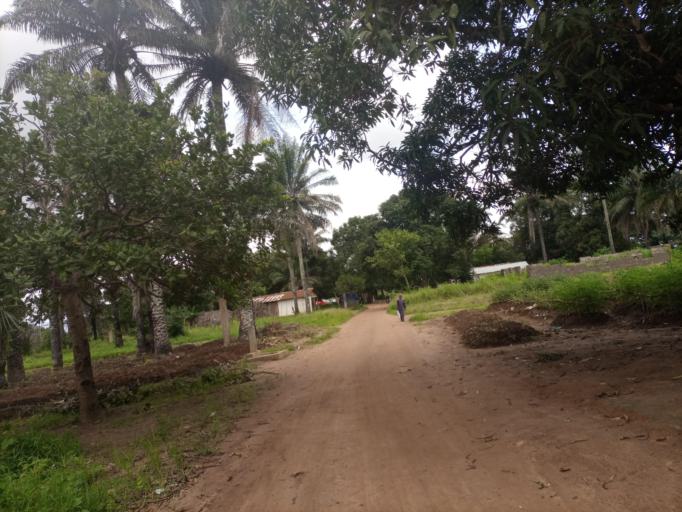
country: SL
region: Northern Province
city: Masoyila
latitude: 8.5931
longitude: -13.1638
